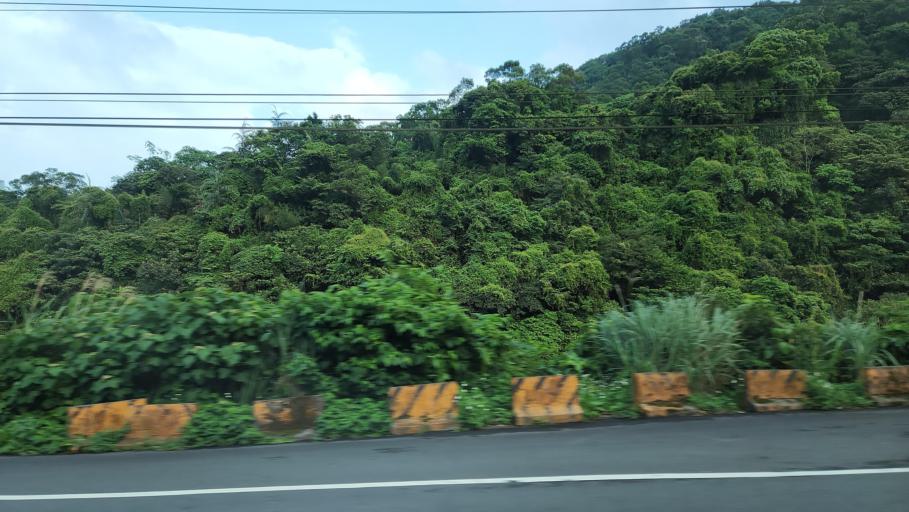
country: TW
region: Taiwan
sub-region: Keelung
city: Keelung
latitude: 25.1646
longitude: 121.6541
